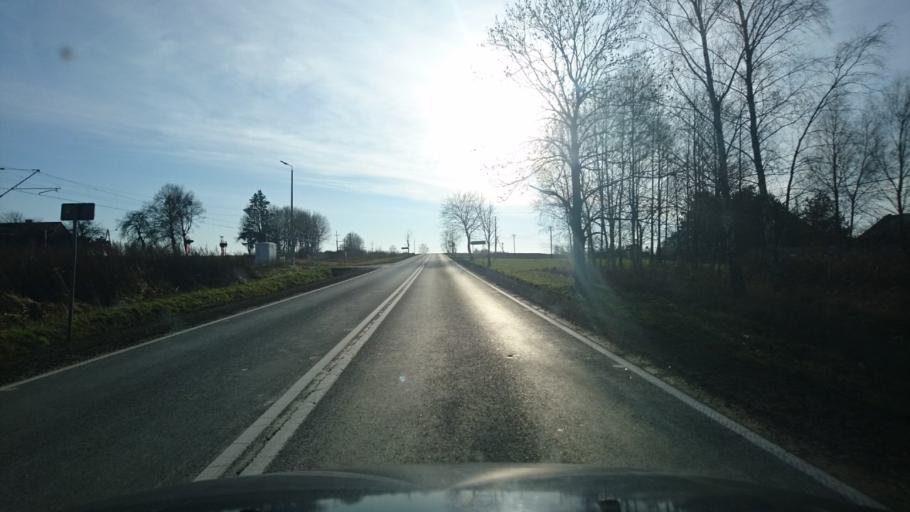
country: PL
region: Opole Voivodeship
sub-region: Powiat oleski
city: Dalachow
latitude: 51.0652
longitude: 18.6007
